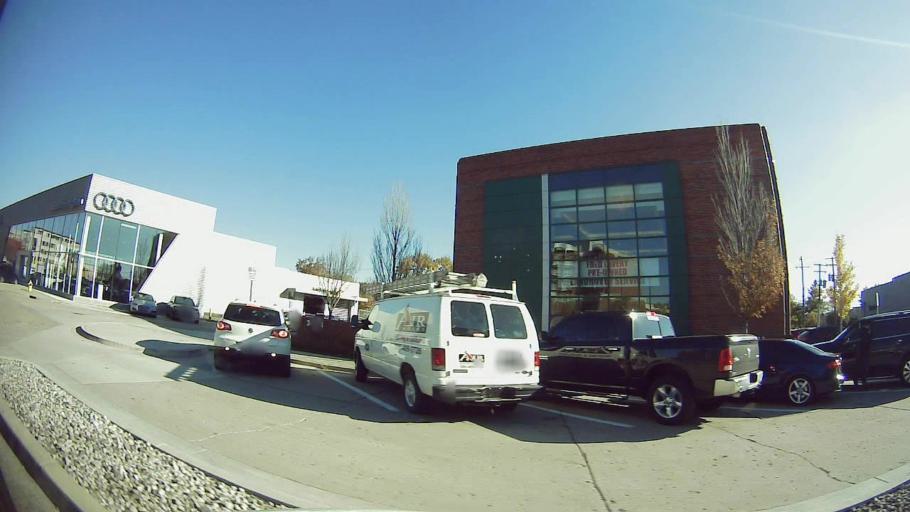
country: US
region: Michigan
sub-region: Oakland County
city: Birmingham
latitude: 42.5438
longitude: -83.2095
